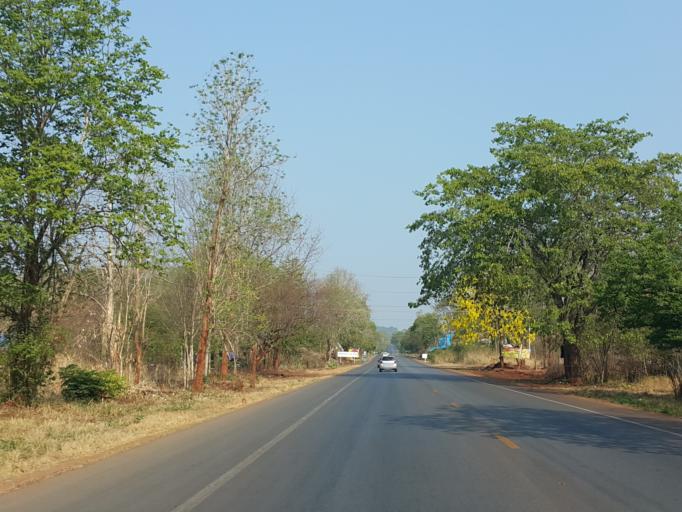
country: TH
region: Kanchanaburi
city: Sai Yok
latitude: 14.1010
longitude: 99.2295
